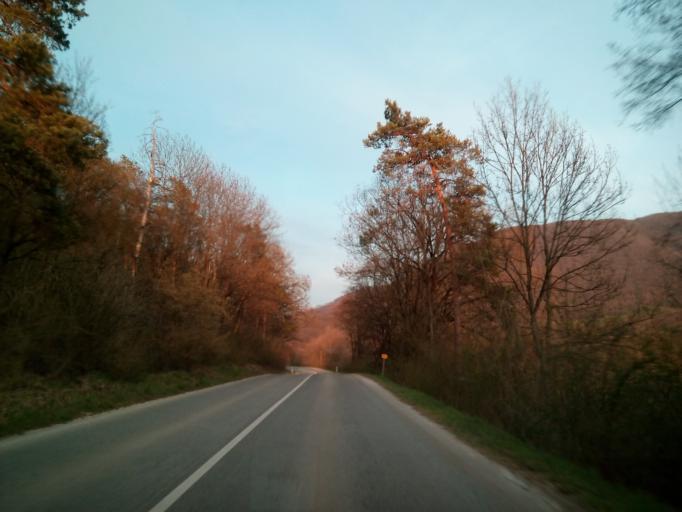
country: SK
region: Kosicky
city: Roznava
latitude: 48.6628
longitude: 20.3848
